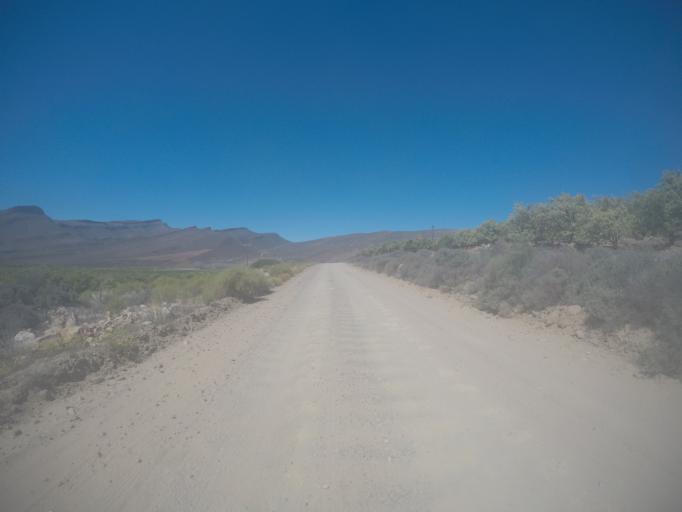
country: ZA
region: Western Cape
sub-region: West Coast District Municipality
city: Clanwilliam
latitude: -32.5576
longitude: 19.3615
